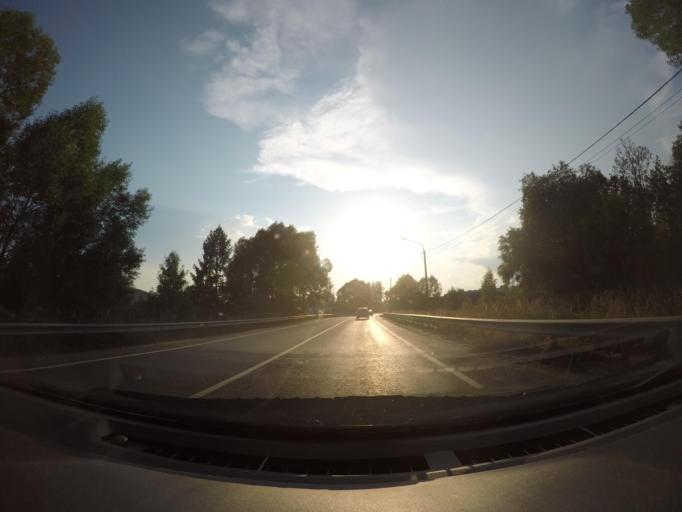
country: RU
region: Moskovskaya
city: Gzhel'
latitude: 55.6065
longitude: 38.4036
